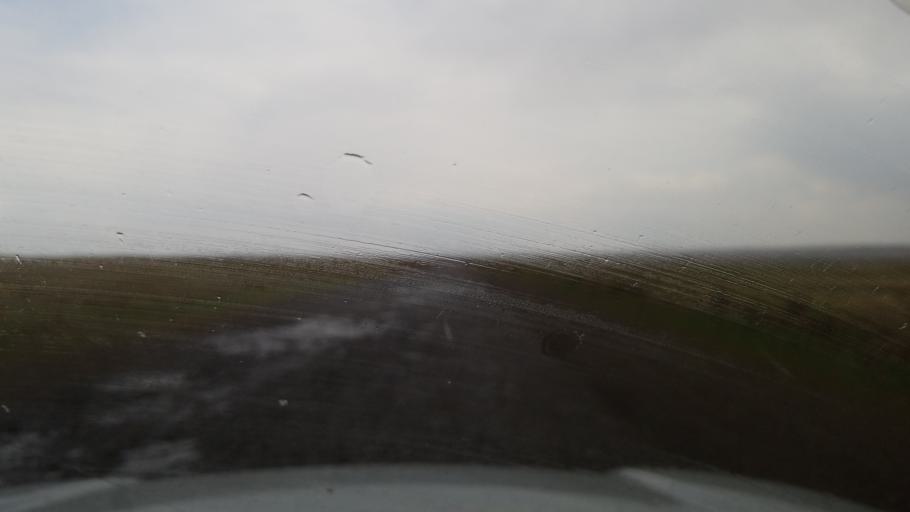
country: TM
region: Mary
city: Serhetabat
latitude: 35.8796
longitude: 62.6201
